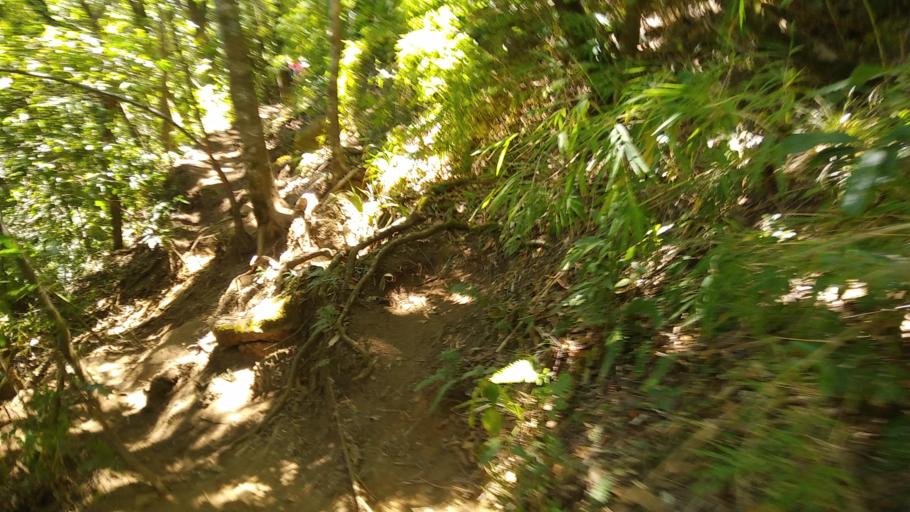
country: CR
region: Alajuela
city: Sabanilla
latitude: 10.1485
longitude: -84.2425
